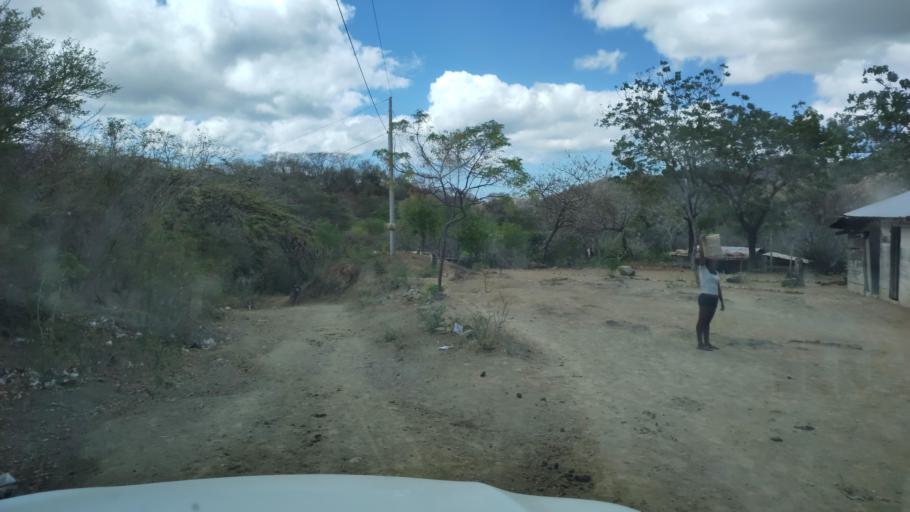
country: NI
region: Carazo
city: Santa Teresa
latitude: 11.6399
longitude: -86.2213
